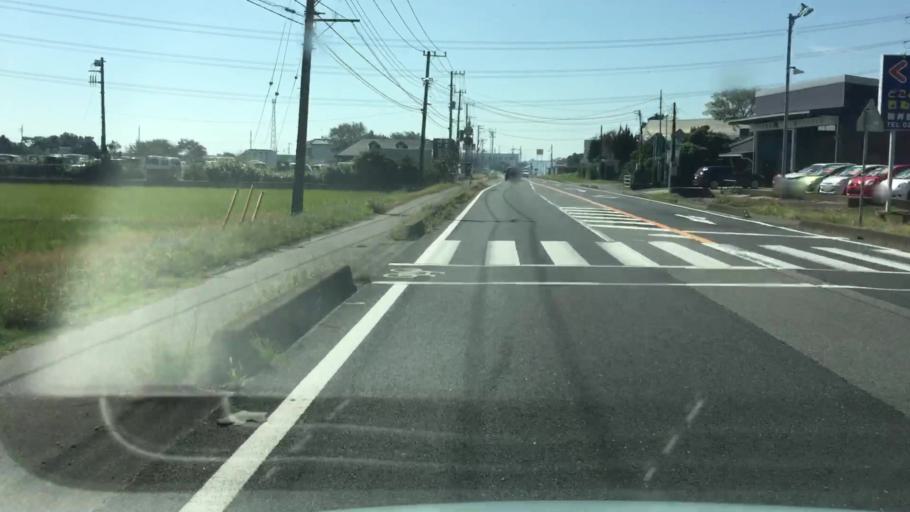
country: JP
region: Ibaraki
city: Ryugasaki
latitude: 35.8703
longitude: 140.1543
